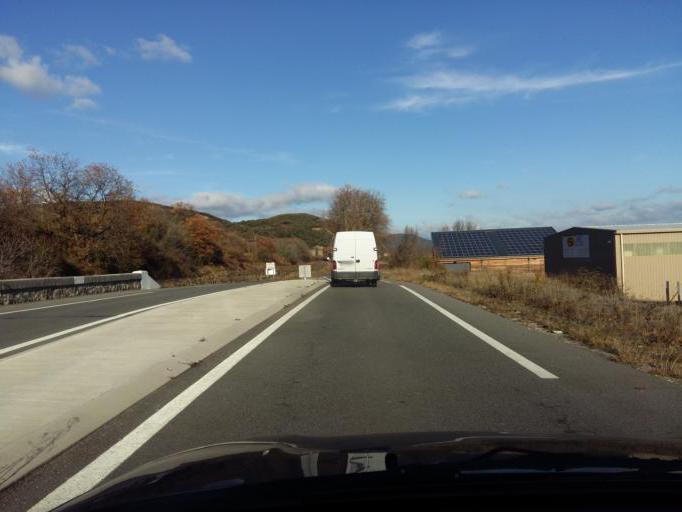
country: FR
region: Rhone-Alpes
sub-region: Departement de l'Ardeche
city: Bourg-Saint-Andeol
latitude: 44.3986
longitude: 4.6446
